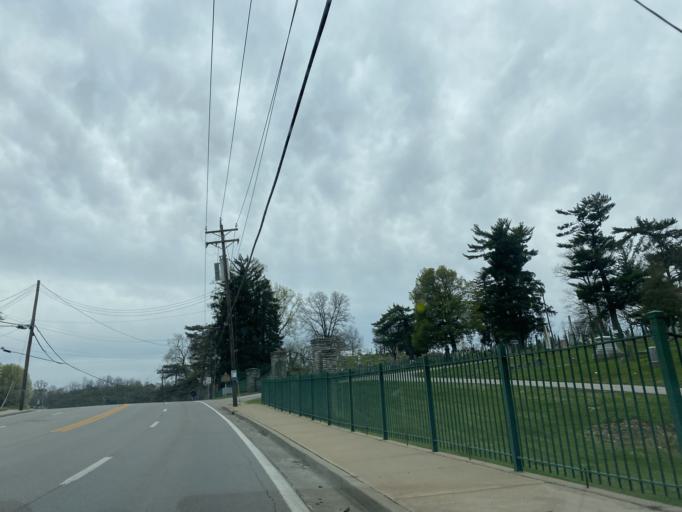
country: US
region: Kentucky
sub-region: Campbell County
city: Southgate
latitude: 39.0700
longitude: -84.4692
